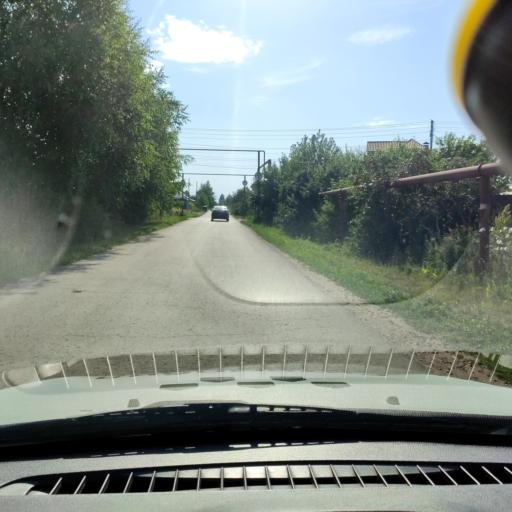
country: RU
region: Samara
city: Podstepki
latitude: 53.5182
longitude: 49.1860
